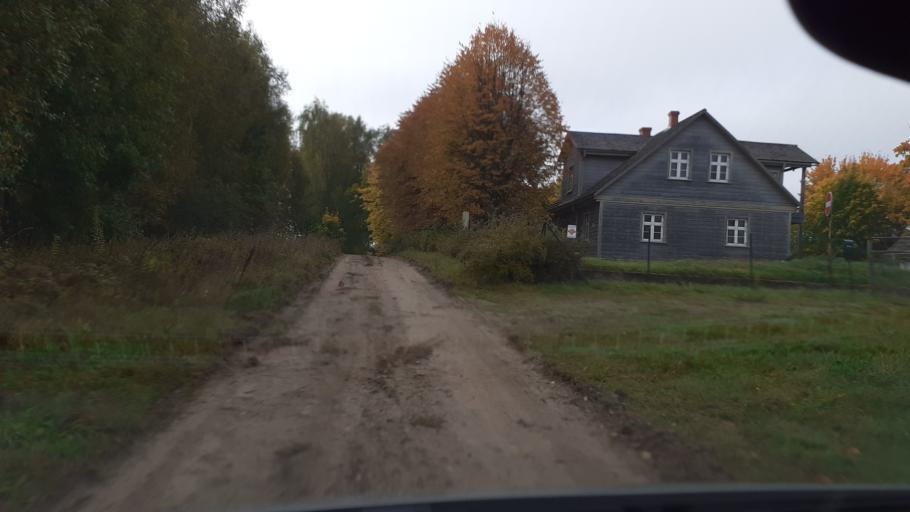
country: LV
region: Kuldigas Rajons
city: Kuldiga
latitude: 56.9738
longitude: 21.9392
